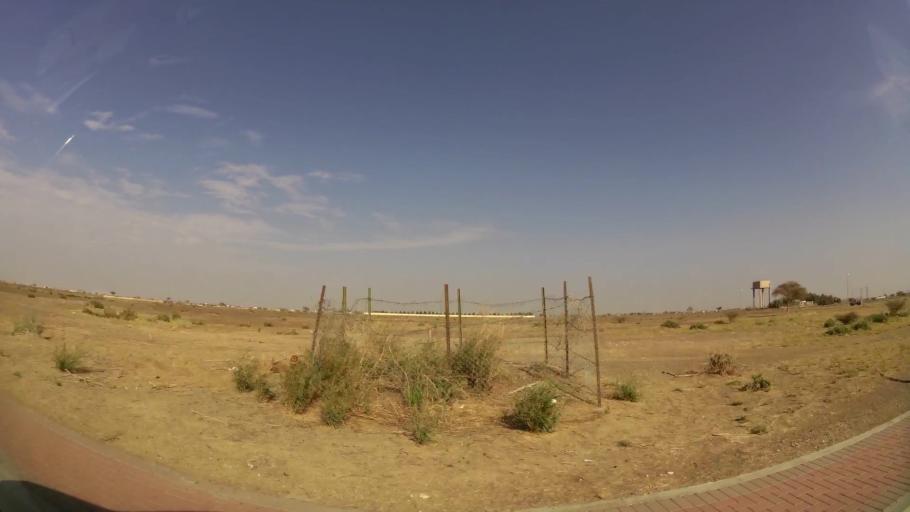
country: AE
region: Abu Dhabi
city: Al Ain
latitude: 24.0413
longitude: 55.8525
